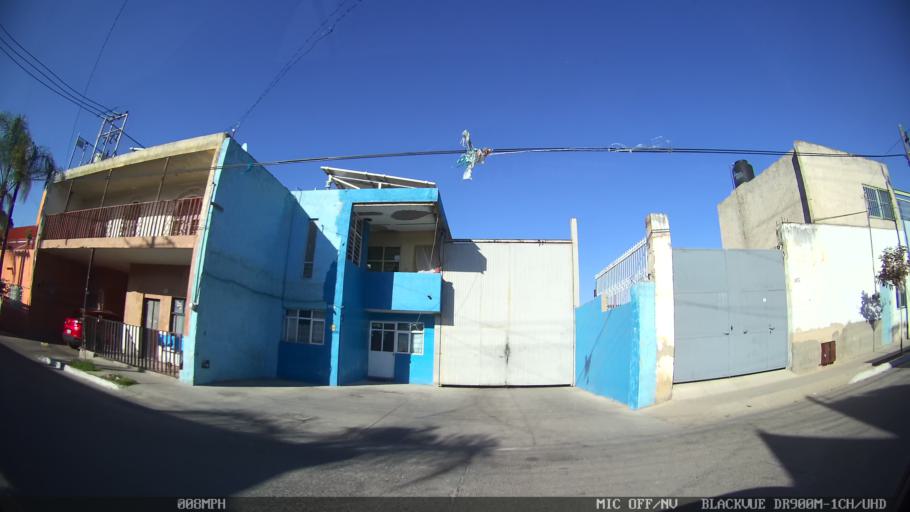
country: MX
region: Jalisco
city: Tlaquepaque
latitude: 20.7086
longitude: -103.2982
